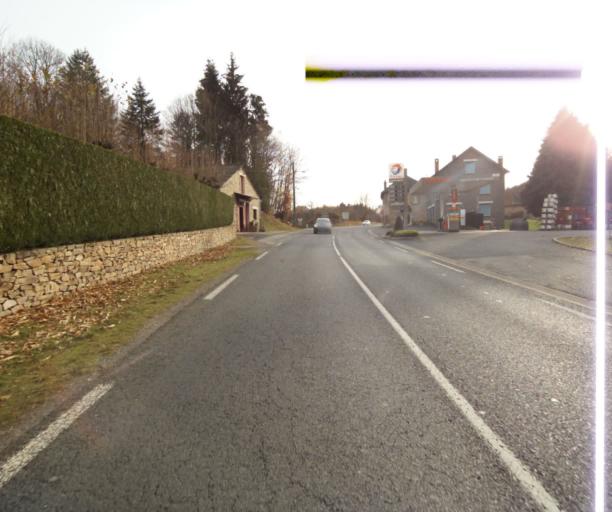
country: FR
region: Limousin
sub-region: Departement de la Correze
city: Sainte-Fortunade
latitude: 45.1966
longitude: 1.7741
